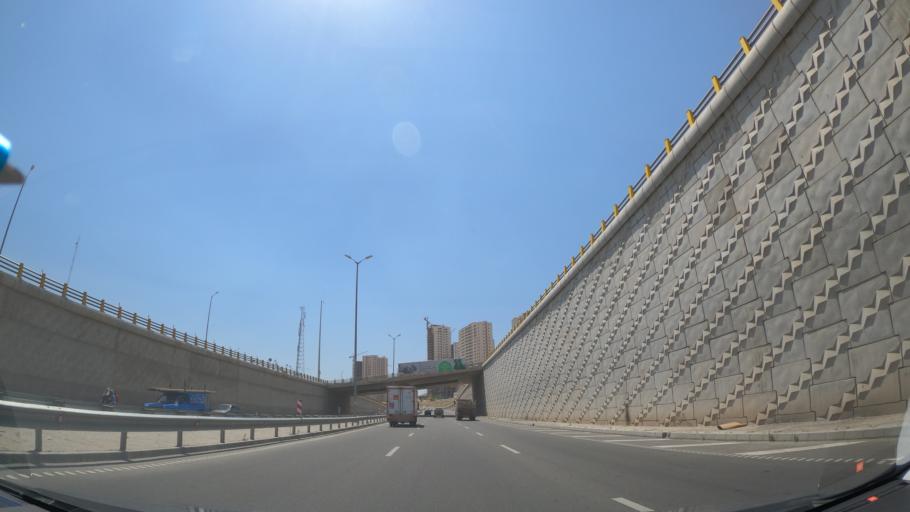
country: IR
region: Tehran
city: Shahr-e Qods
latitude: 35.7523
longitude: 51.1450
